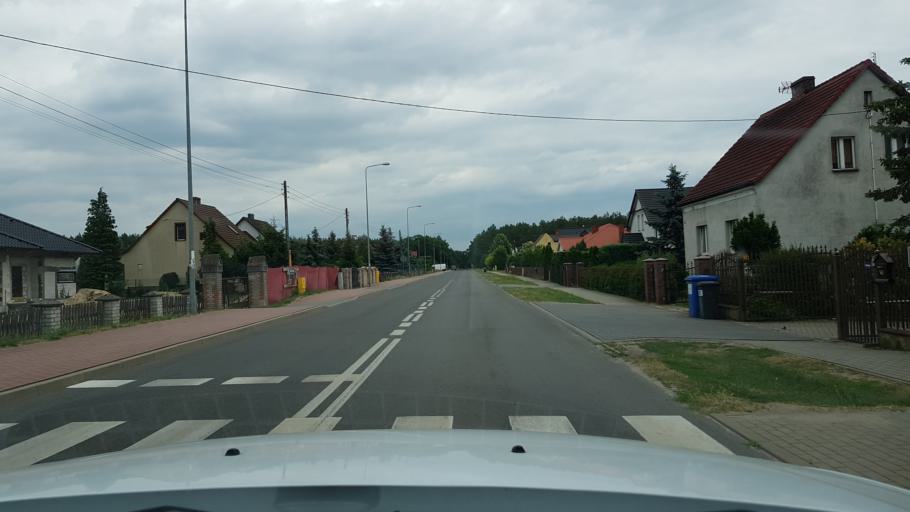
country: PL
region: Lubusz
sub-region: Powiat gorzowski
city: Kostrzyn nad Odra
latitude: 52.6223
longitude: 14.5931
